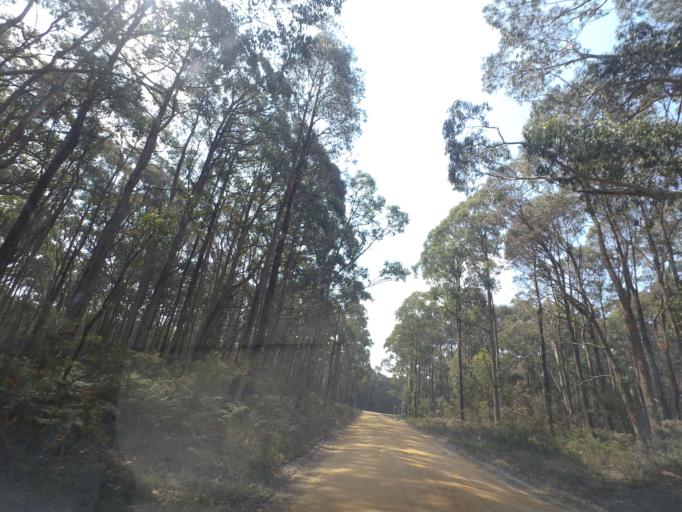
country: AU
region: Victoria
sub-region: Moorabool
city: Bacchus Marsh
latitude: -37.4312
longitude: 144.3479
